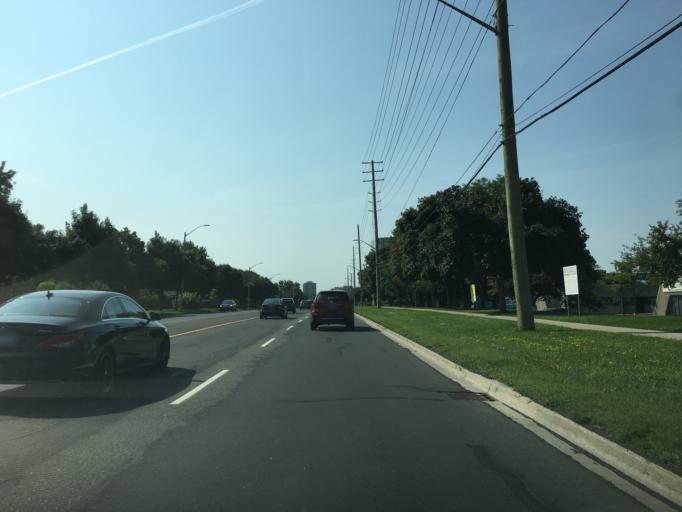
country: CA
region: Ontario
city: Markham
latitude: 43.8264
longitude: -79.3264
